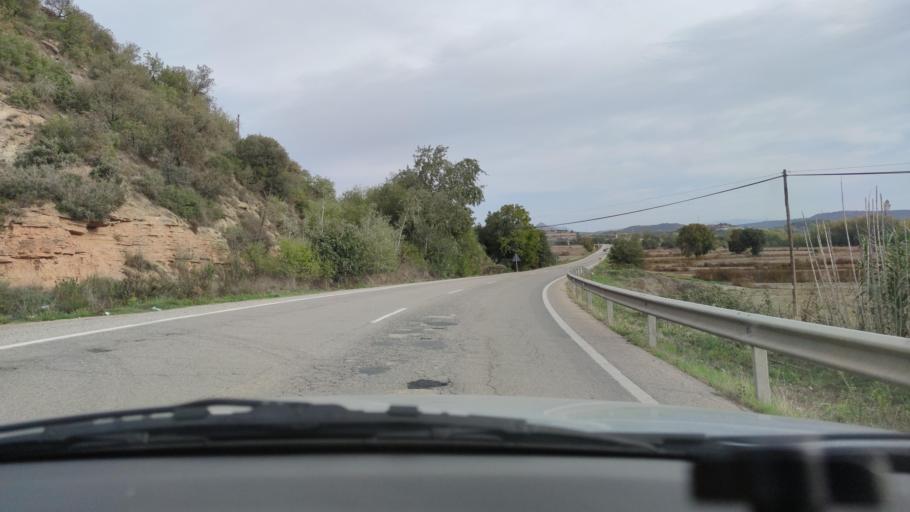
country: ES
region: Catalonia
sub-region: Provincia de Lleida
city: Artesa de Segre
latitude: 41.9122
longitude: 1.0679
